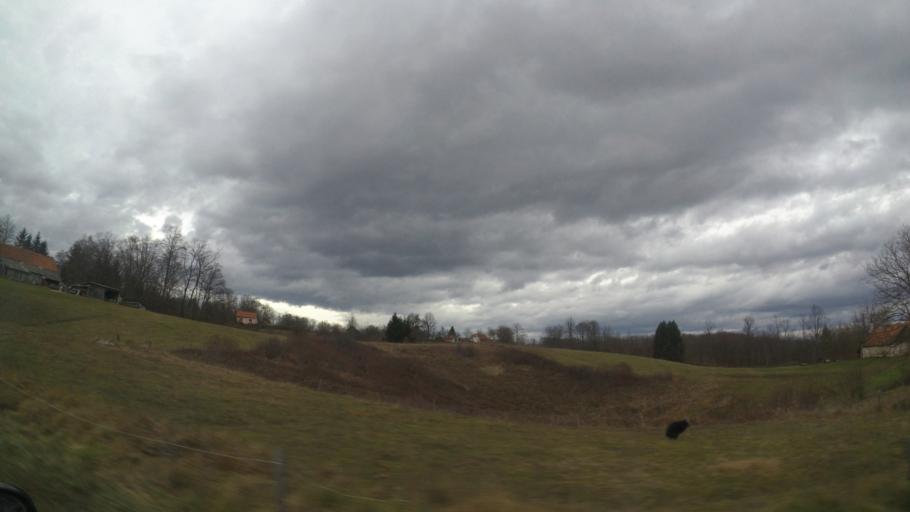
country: HR
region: Karlovacka
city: Vojnic
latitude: 45.3461
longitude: 15.5877
